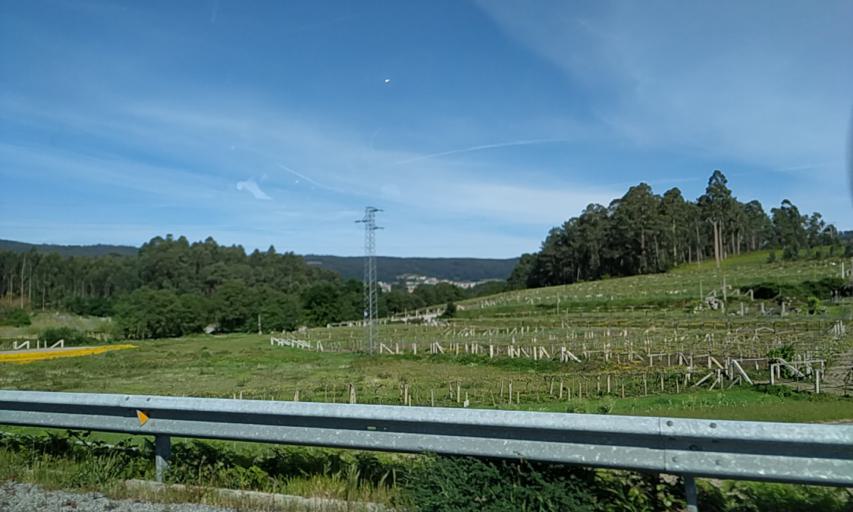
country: ES
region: Galicia
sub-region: Provincia de Pontevedra
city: Meano
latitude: 42.4350
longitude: -8.8035
